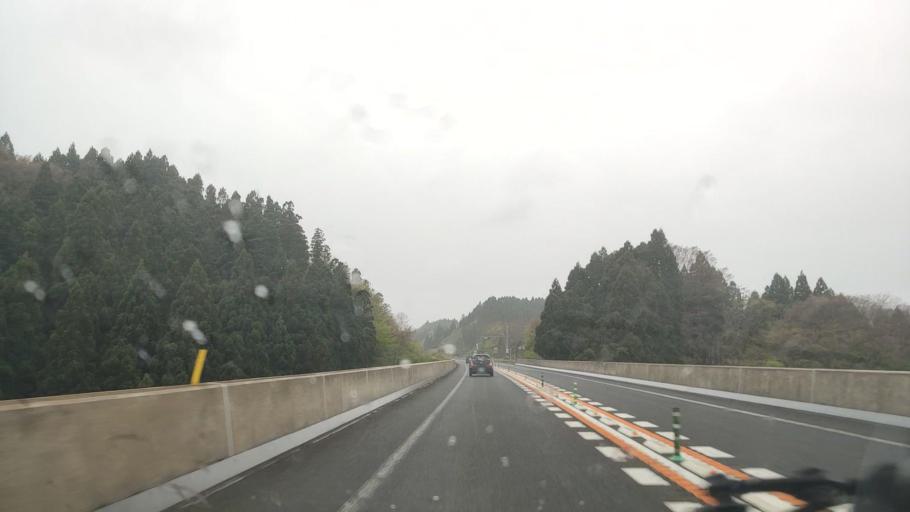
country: JP
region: Akita
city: Noshiromachi
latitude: 40.1996
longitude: 140.1316
